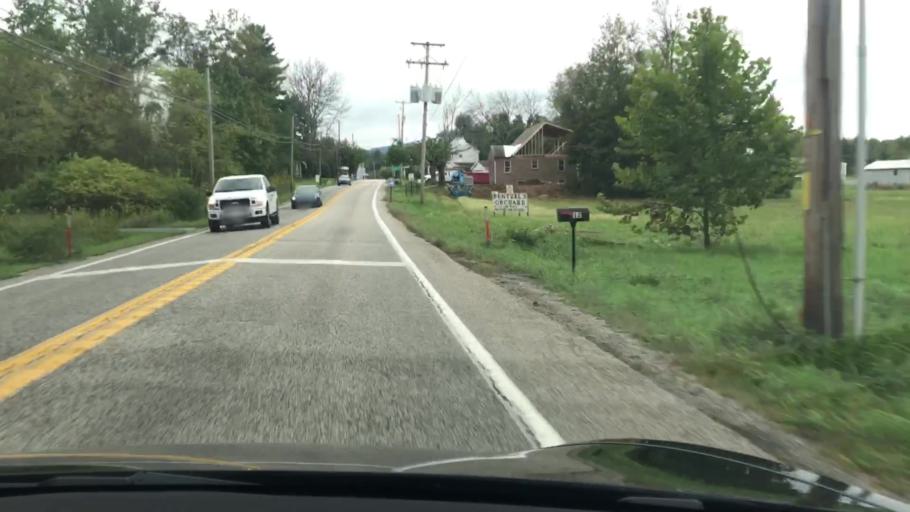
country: US
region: Pennsylvania
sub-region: Cumberland County
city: Shiremanstown
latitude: 40.1478
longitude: -76.9662
